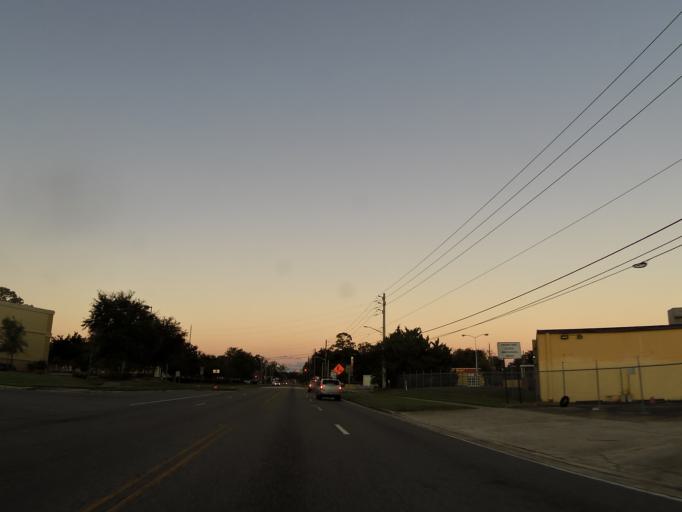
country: US
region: Florida
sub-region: Duval County
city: Jacksonville
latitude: 30.3145
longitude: -81.7324
